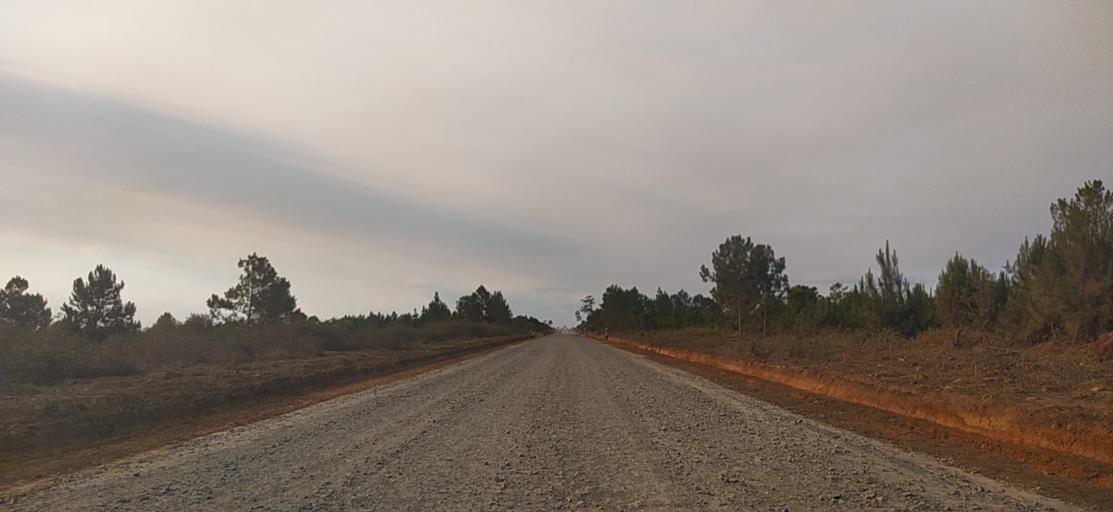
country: MG
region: Alaotra Mangoro
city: Moramanga
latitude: -18.5417
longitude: 48.2594
